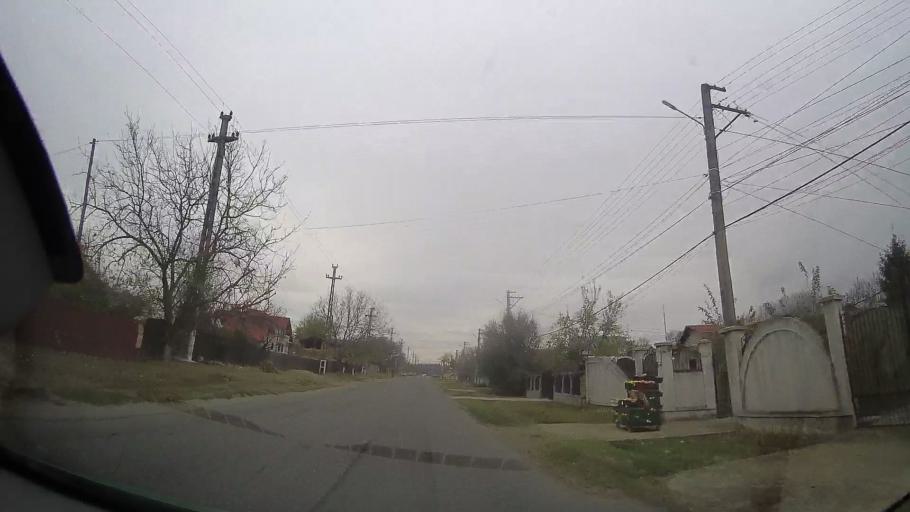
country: RO
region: Prahova
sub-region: Oras Urlati
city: Urlati
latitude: 45.0028
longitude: 26.2274
